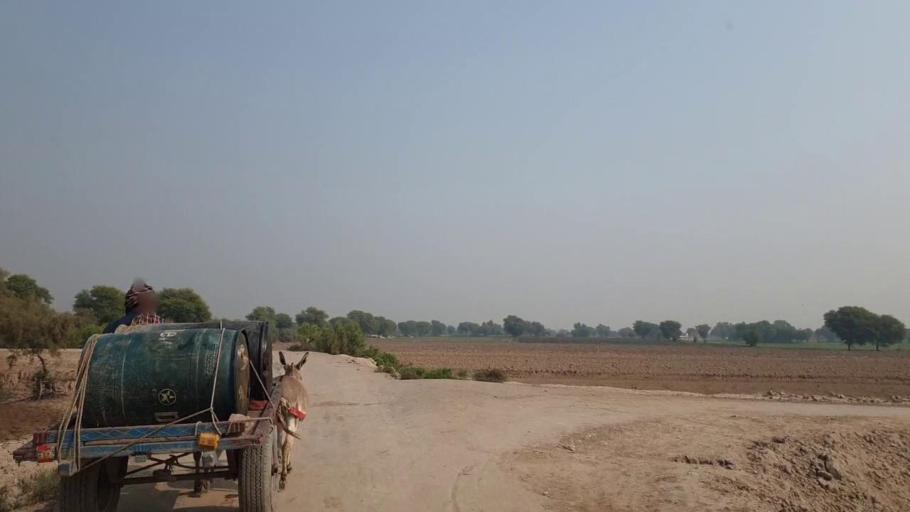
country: PK
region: Sindh
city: Bhan
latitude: 26.5178
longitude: 67.7281
